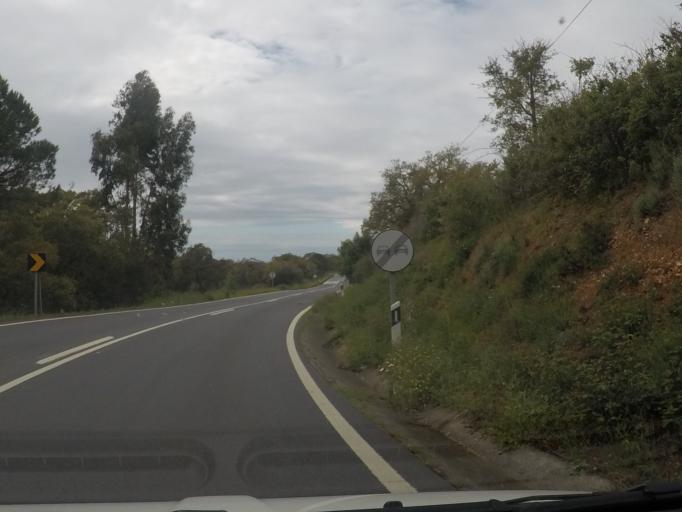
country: PT
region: Setubal
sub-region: Sines
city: Porto Covo
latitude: 37.8689
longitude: -8.7410
